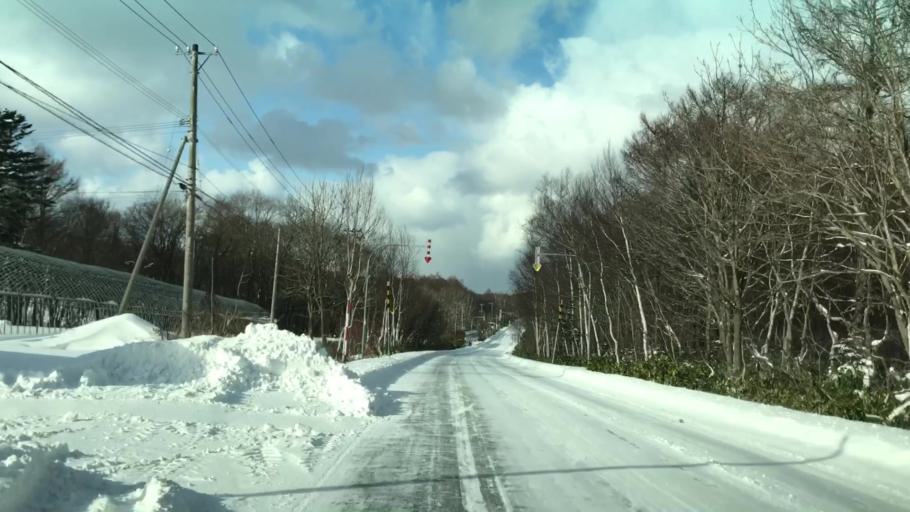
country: JP
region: Hokkaido
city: Yoichi
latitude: 43.3172
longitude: 140.5310
